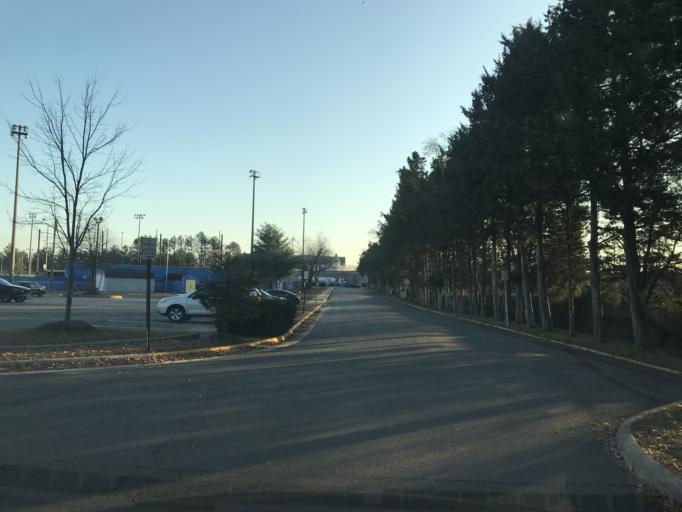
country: US
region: Virginia
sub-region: Fairfax County
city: Springfield
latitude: 38.7799
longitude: -77.1711
